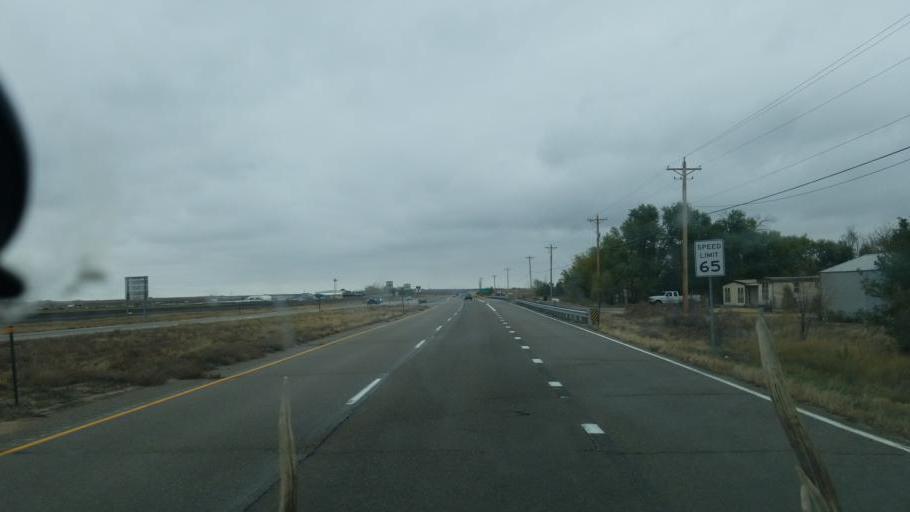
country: US
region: Colorado
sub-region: Pueblo County
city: Pueblo
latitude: 38.2742
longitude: -104.4561
